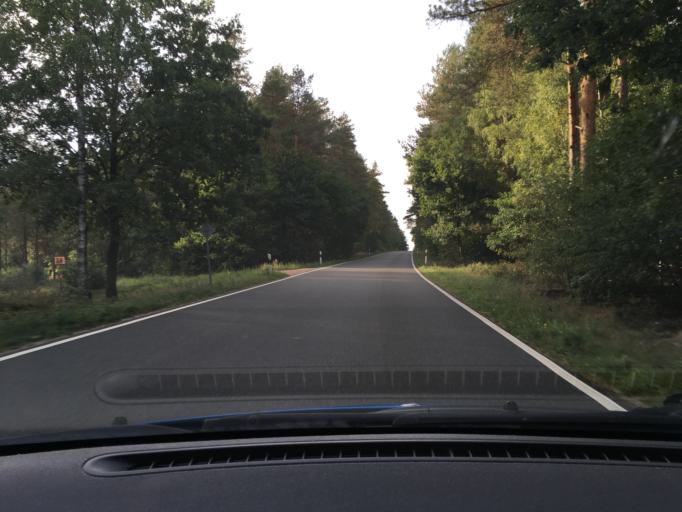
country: DE
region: Lower Saxony
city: Fassberg
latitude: 52.9007
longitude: 10.1078
